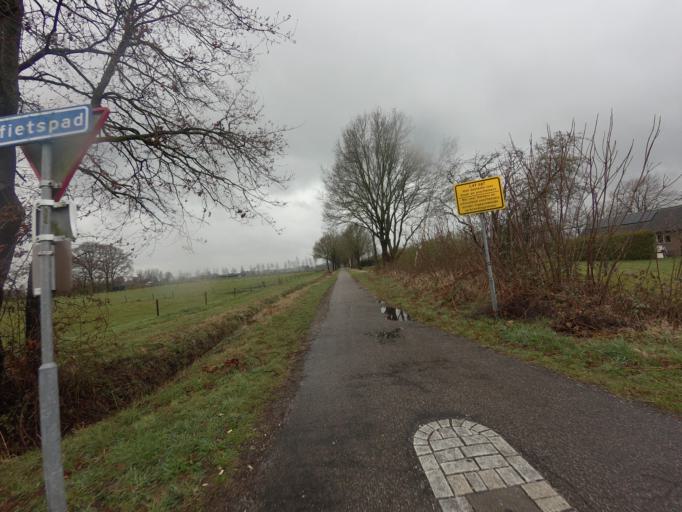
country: NL
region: Gelderland
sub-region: Gemeente Epe
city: Vaassen
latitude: 52.2731
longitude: 5.9699
